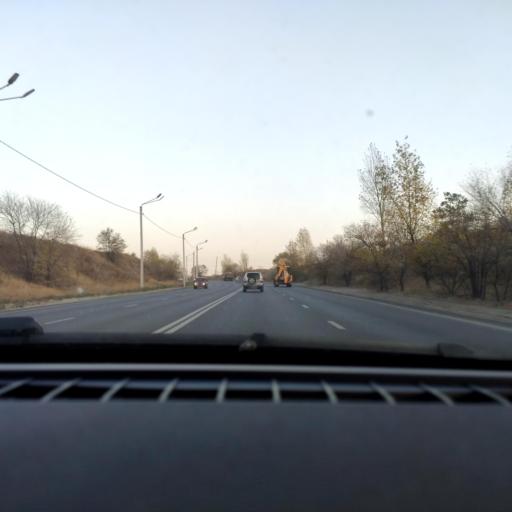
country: RU
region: Voronezj
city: Maslovka
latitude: 51.6213
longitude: 39.2679
